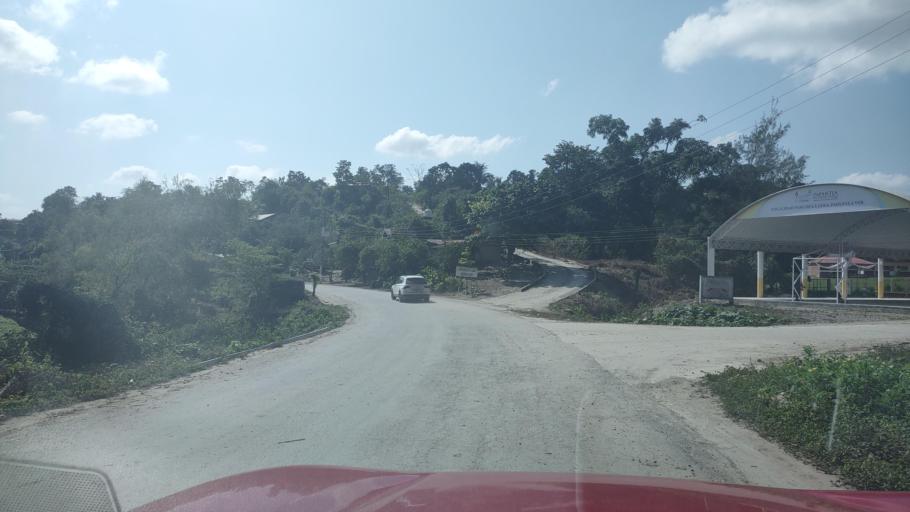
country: MX
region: Veracruz
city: Agua Dulce
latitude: 20.2952
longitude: -97.1493
